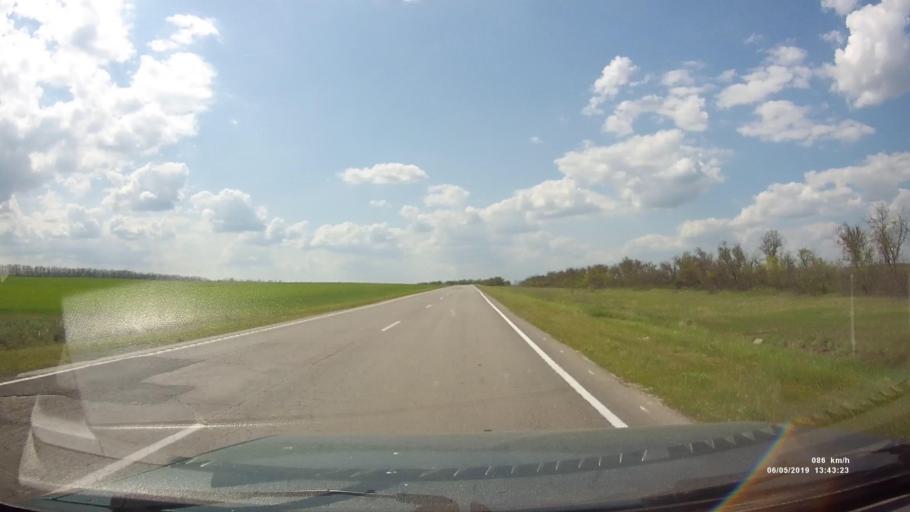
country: RU
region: Rostov
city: Semikarakorsk
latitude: 47.6604
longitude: 40.6394
